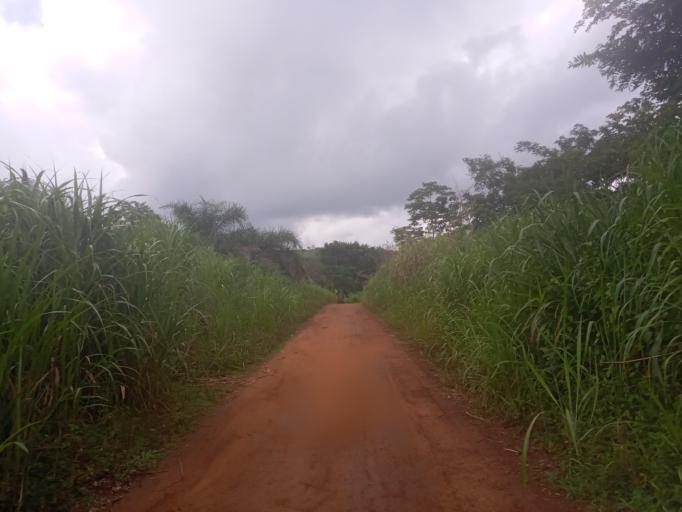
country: SL
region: Northern Province
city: Bumbuna
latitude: 8.9276
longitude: -11.7448
